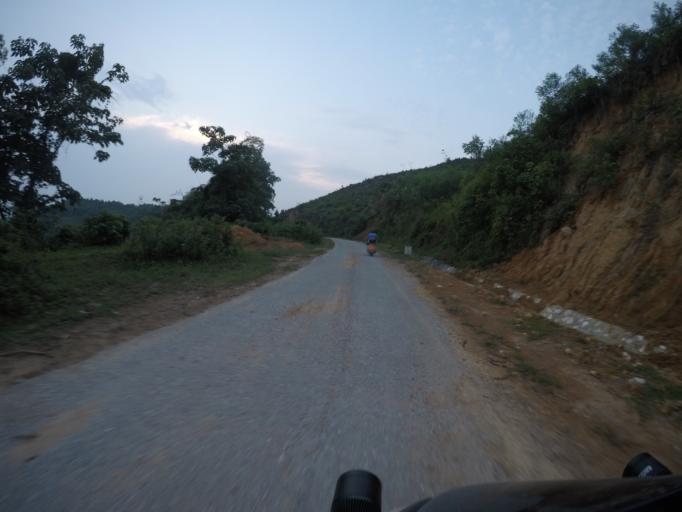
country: VN
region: Thai Nguyen
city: Chua Hang
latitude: 21.5838
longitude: 105.7121
